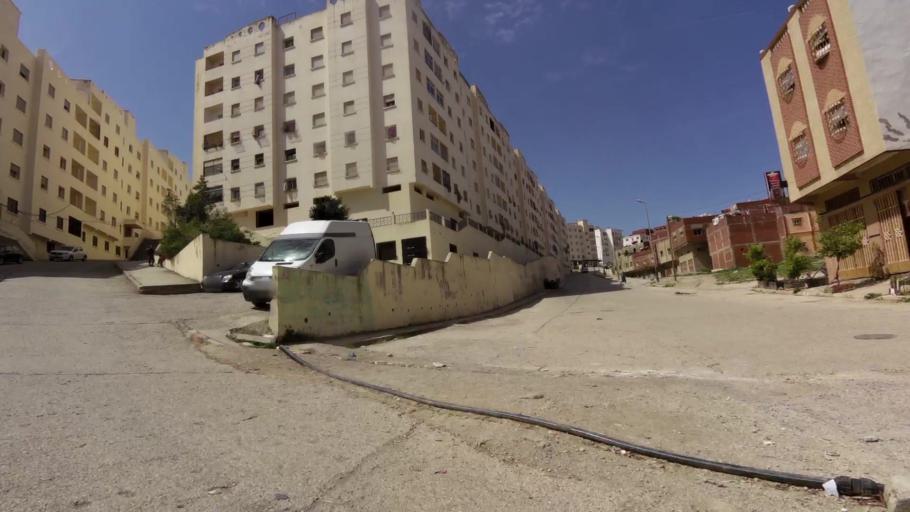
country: MA
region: Tanger-Tetouan
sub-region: Tanger-Assilah
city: Tangier
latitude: 35.7329
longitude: -5.8127
